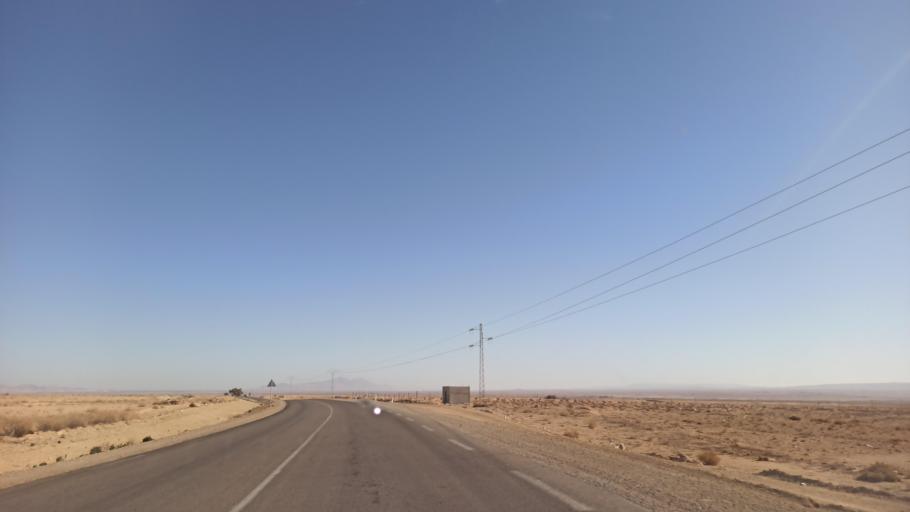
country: TN
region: Gafsa
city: Al Metlaoui
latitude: 34.3136
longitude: 8.4931
